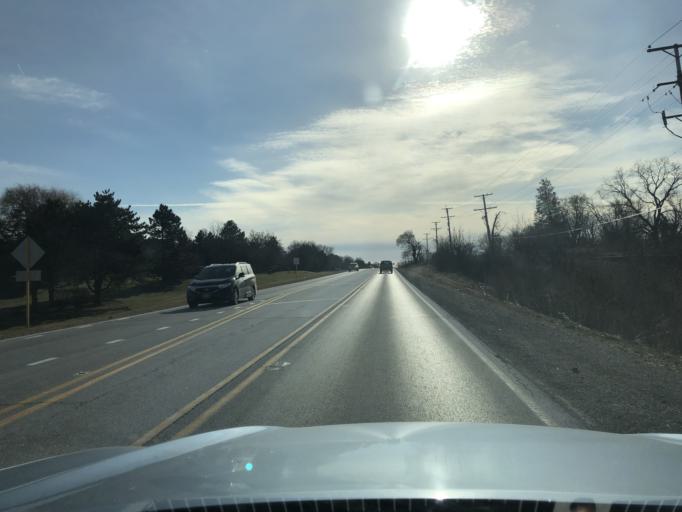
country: US
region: Illinois
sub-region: Lake County
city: Grandwood Park
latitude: 42.4019
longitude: -88.0042
